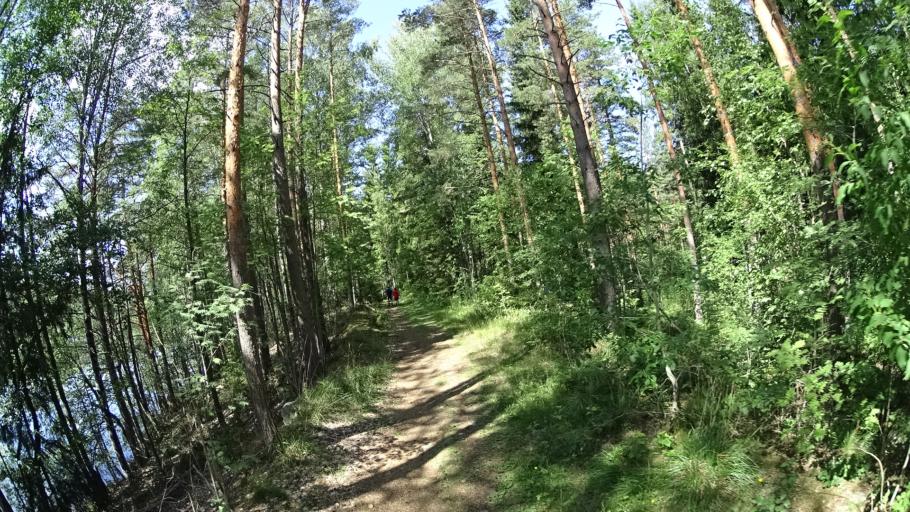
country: FI
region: Haeme
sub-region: Forssa
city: Tammela
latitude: 60.7701
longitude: 23.8694
